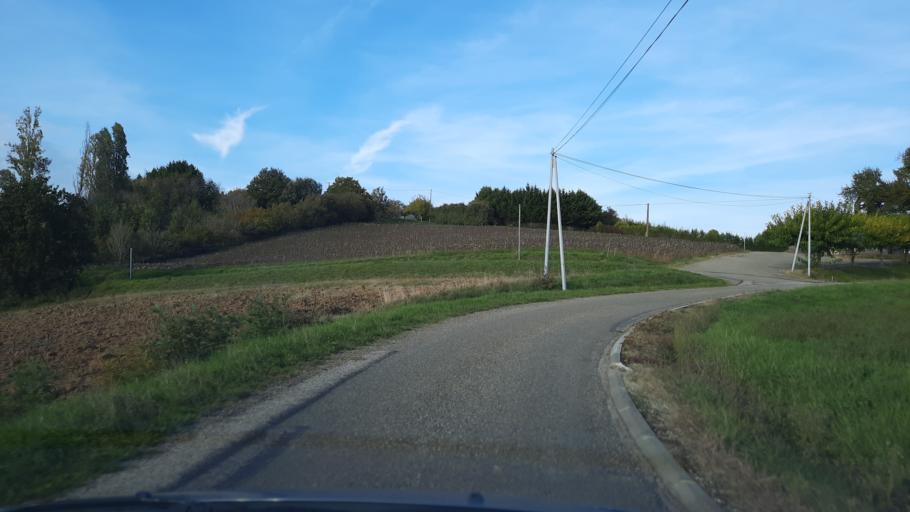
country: FR
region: Midi-Pyrenees
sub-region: Departement du Tarn-et-Garonne
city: Molieres
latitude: 44.1942
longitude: 1.3113
